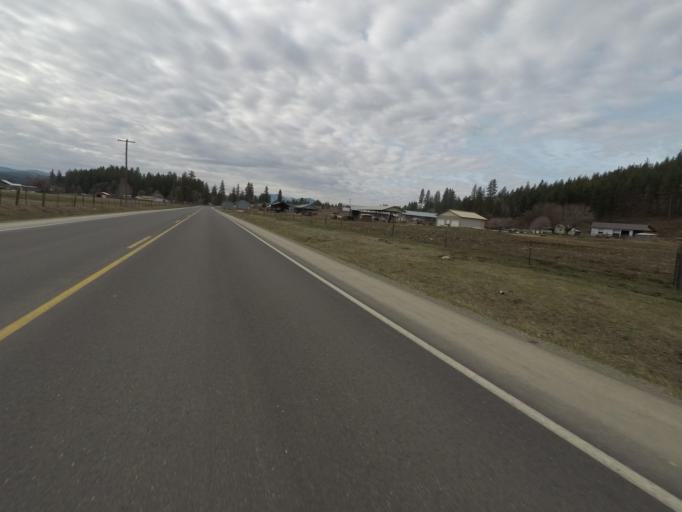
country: US
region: Washington
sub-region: Stevens County
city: Colville
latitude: 48.5614
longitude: -117.8798
